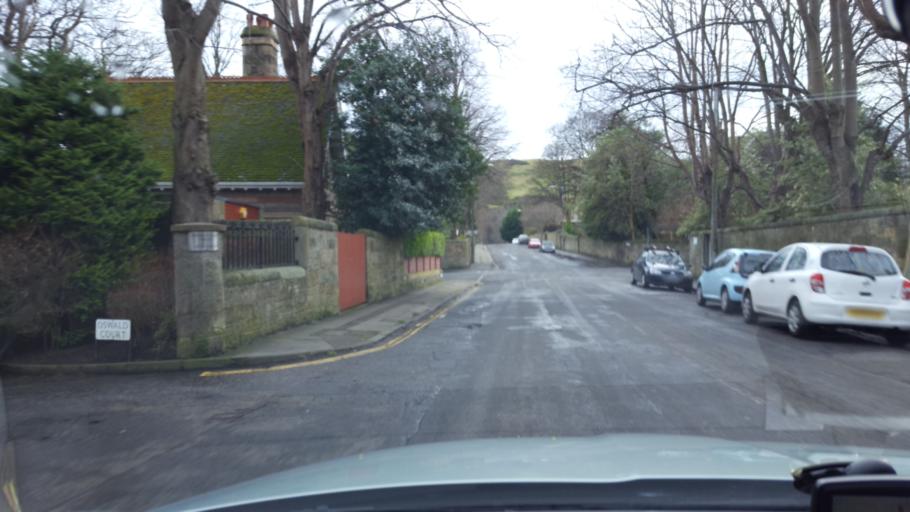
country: GB
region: Scotland
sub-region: Edinburgh
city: Edinburgh
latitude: 55.9292
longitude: -3.1935
